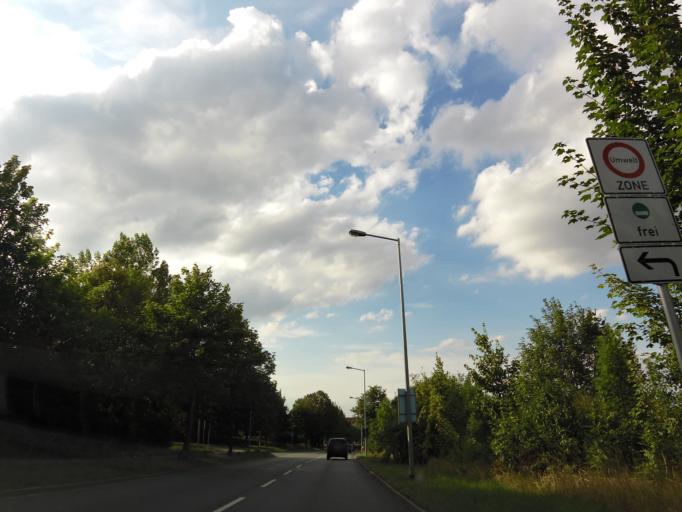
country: DE
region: Thuringia
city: Erfurt
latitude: 50.9618
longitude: 11.0624
